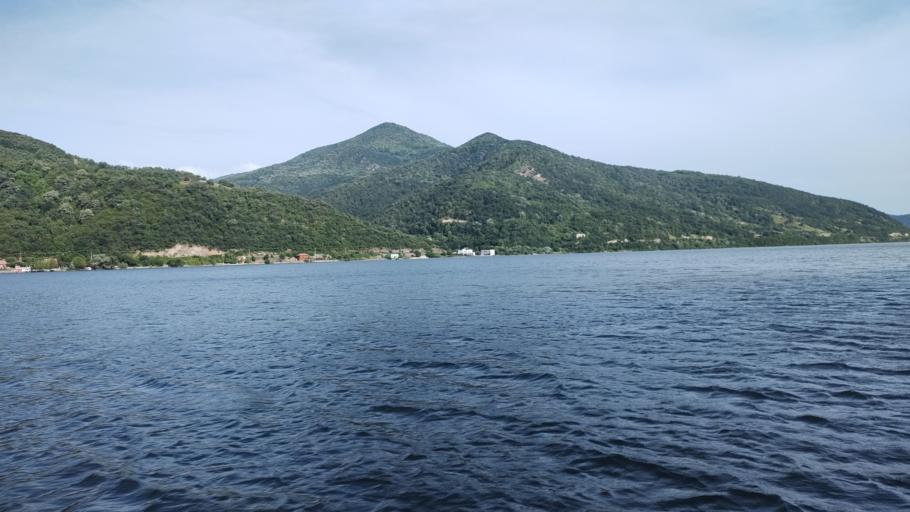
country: RO
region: Caras-Severin
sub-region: Comuna Berzasca
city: Berzasca
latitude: 44.5879
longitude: 22.0246
